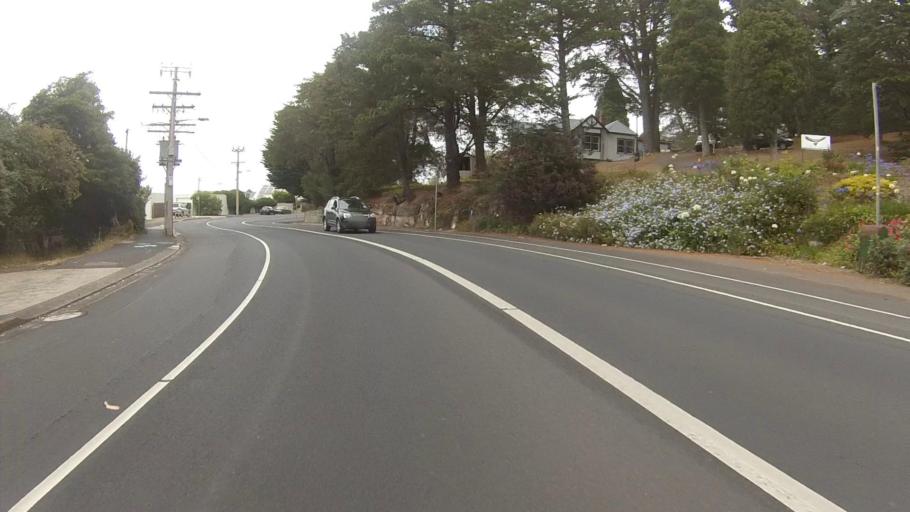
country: AU
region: Tasmania
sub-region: Kingborough
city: Taroona
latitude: -42.9263
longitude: 147.3605
